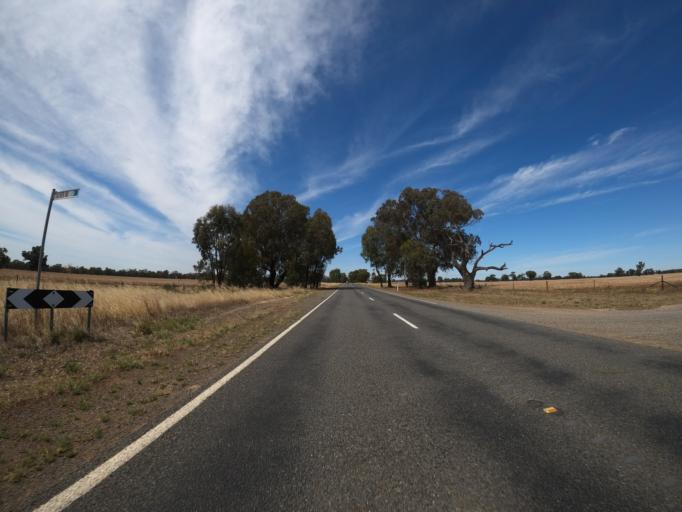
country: AU
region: Victoria
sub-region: Benalla
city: Benalla
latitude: -36.2845
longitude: 145.9523
